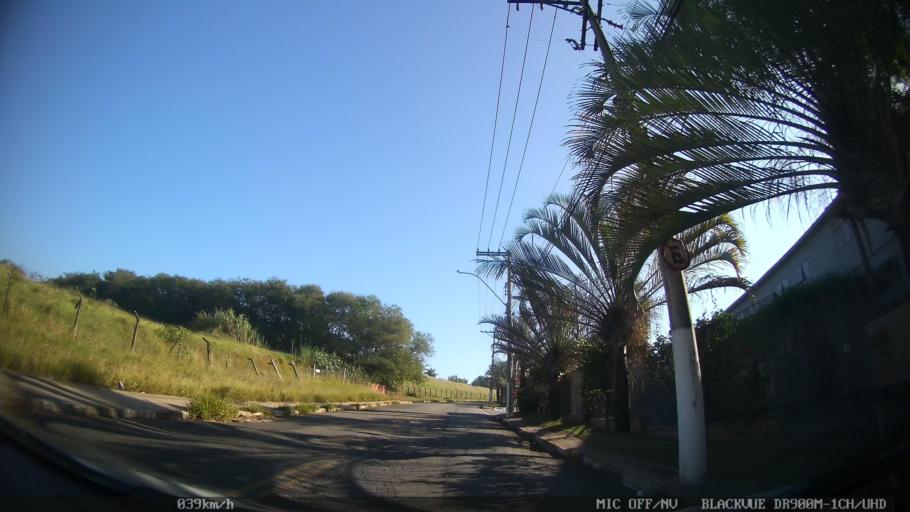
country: BR
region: Sao Paulo
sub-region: Campinas
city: Campinas
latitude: -22.9942
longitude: -47.1116
